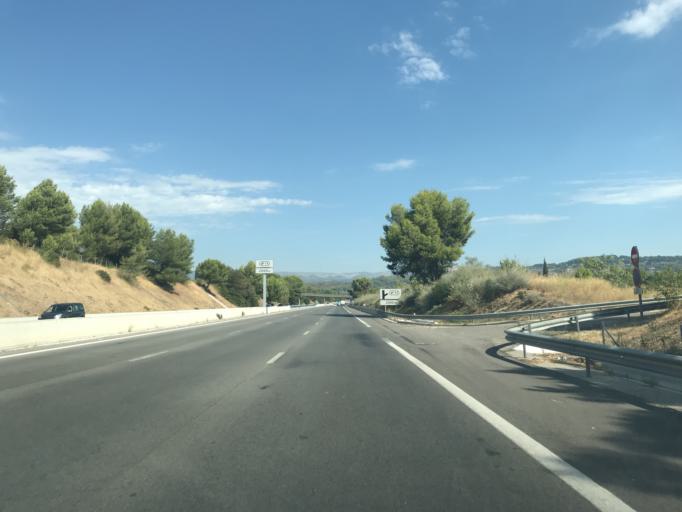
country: FR
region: Provence-Alpes-Cote d'Azur
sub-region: Departement du Var
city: Le Castellet
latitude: 43.1715
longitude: 5.7701
